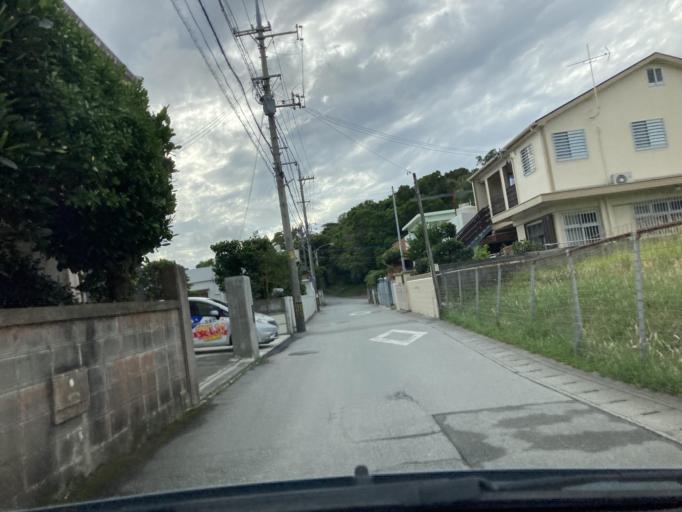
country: JP
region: Okinawa
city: Naha-shi
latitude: 26.2180
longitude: 127.7329
